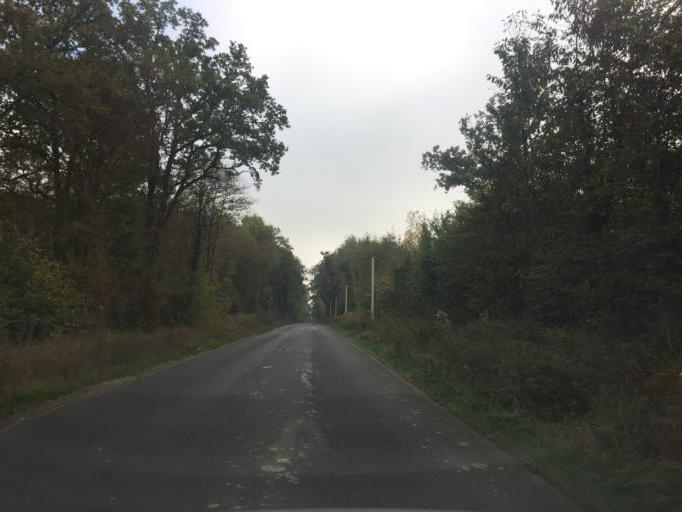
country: FR
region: Rhone-Alpes
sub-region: Departement de l'Ain
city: Saint-Andre-de-Corcy
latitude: 45.9031
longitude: 4.9628
